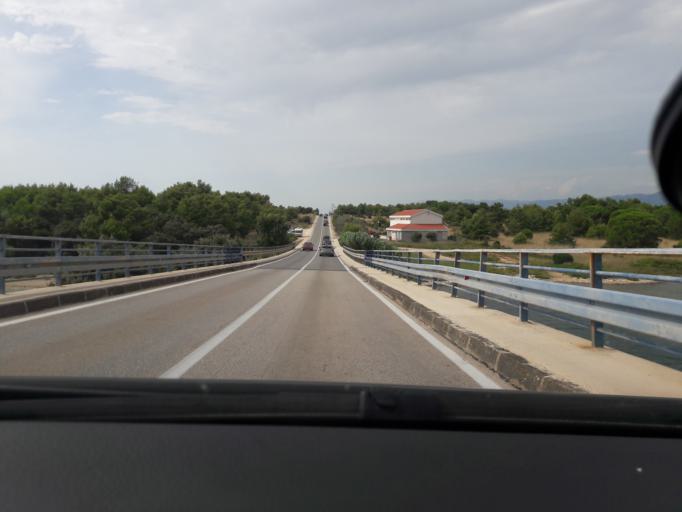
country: HR
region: Zadarska
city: Privlaka
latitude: 44.2809
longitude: 15.1259
